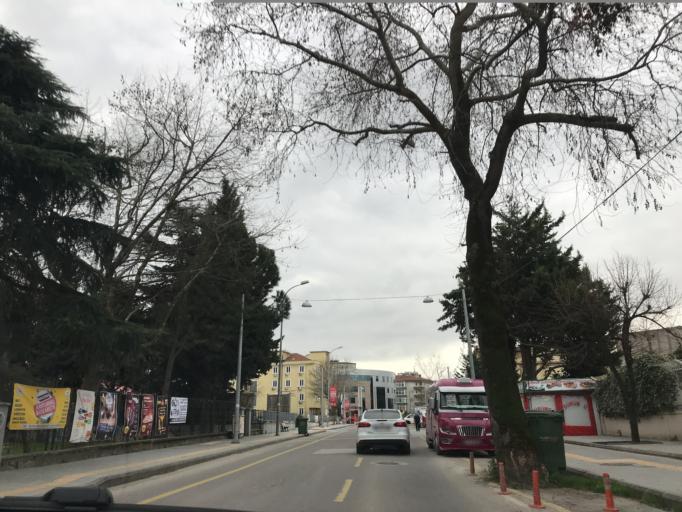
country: TR
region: Yalova
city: Yalova
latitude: 40.6537
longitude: 29.2622
